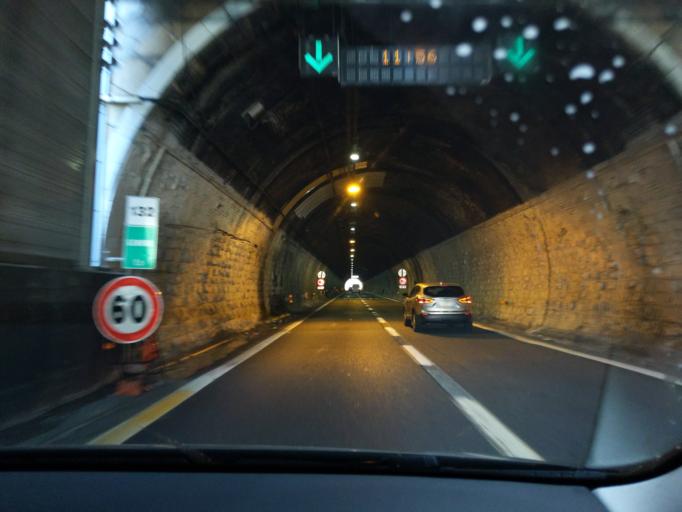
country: IT
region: Liguria
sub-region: Provincia di Genova
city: San Teodoro
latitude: 44.4219
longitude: 8.8952
